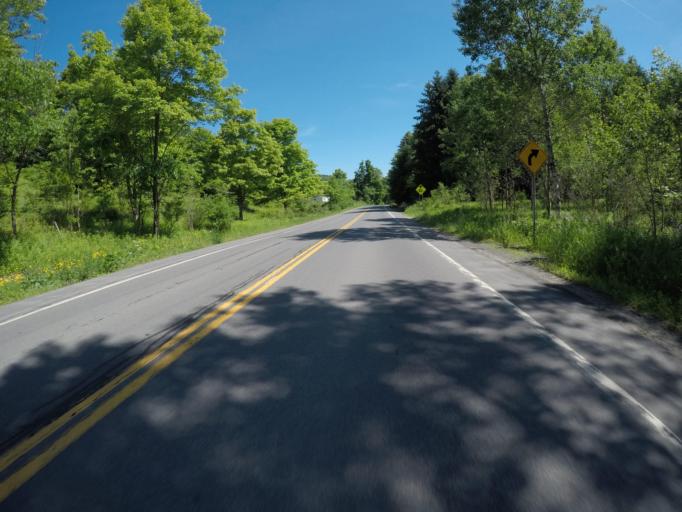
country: US
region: New York
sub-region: Delaware County
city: Delhi
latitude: 42.2370
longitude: -74.9695
